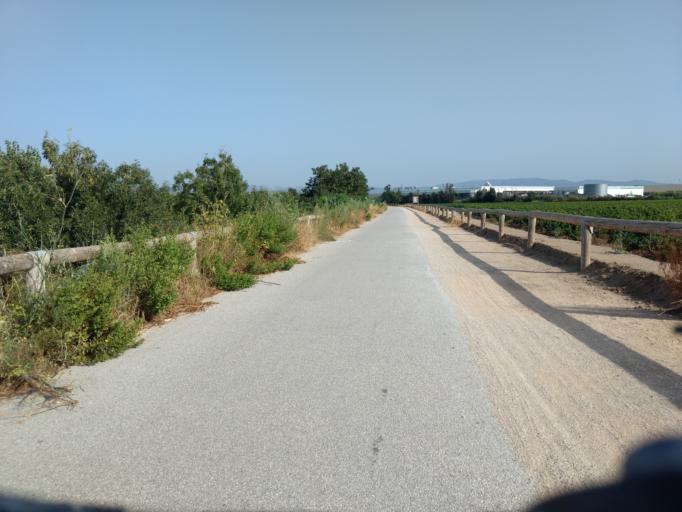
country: FR
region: Languedoc-Roussillon
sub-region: Departement des Pyrenees-Orientales
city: Pia
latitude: 42.7687
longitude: 2.9112
